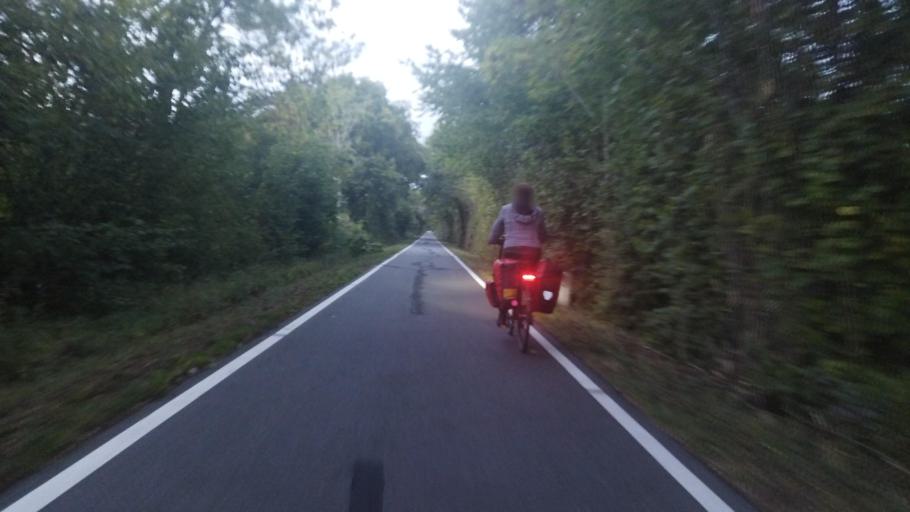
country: DE
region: North Rhine-Westphalia
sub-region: Regierungsbezirk Munster
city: Horstmar
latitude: 52.0822
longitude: 7.3216
